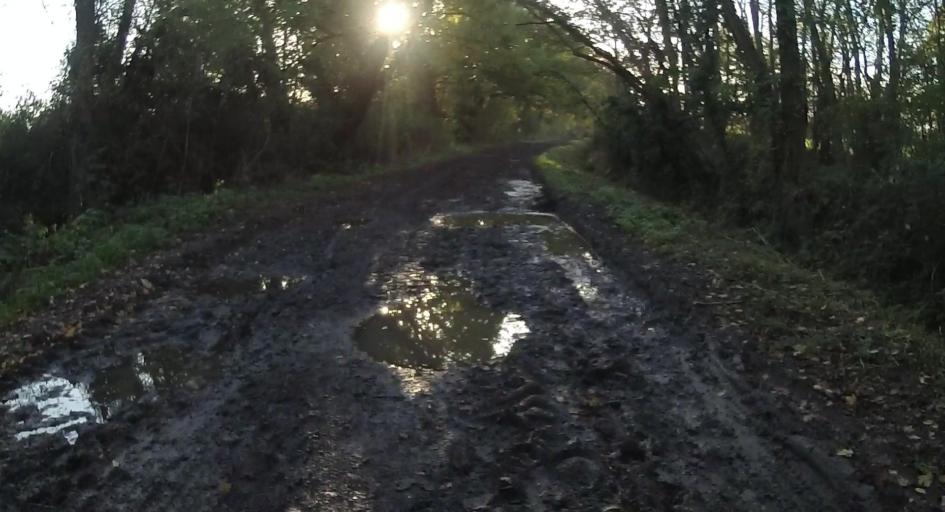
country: GB
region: England
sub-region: West Berkshire
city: Arborfield
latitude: 51.4000
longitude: -0.8991
